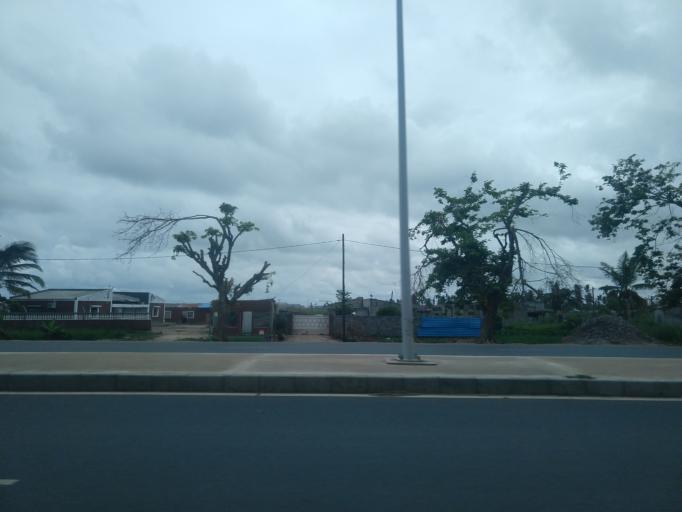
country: MZ
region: Sofala
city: Beira
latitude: -19.7865
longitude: 34.8757
